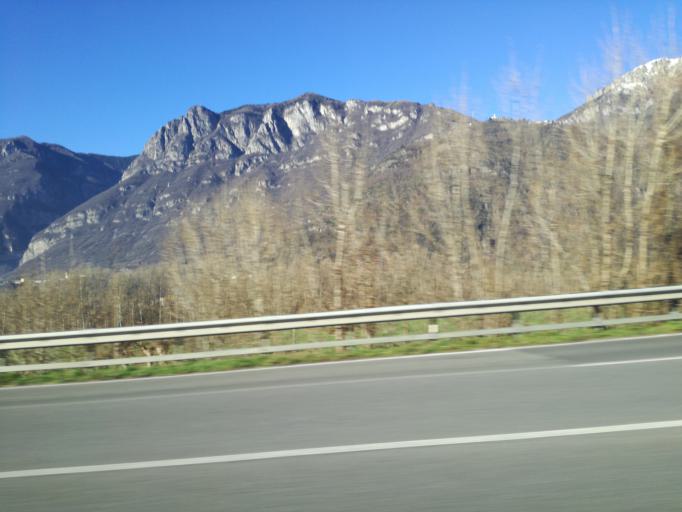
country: IT
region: Lombardy
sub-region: Provincia di Brescia
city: Pian Camuno
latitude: 45.8466
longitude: 10.1372
